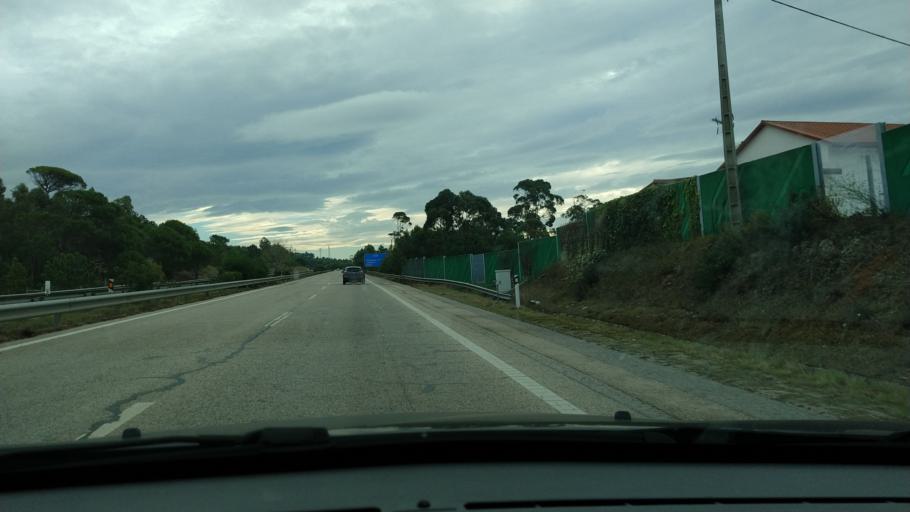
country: PT
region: Coimbra
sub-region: Figueira da Foz
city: Tavarede
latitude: 40.1496
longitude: -8.8270
